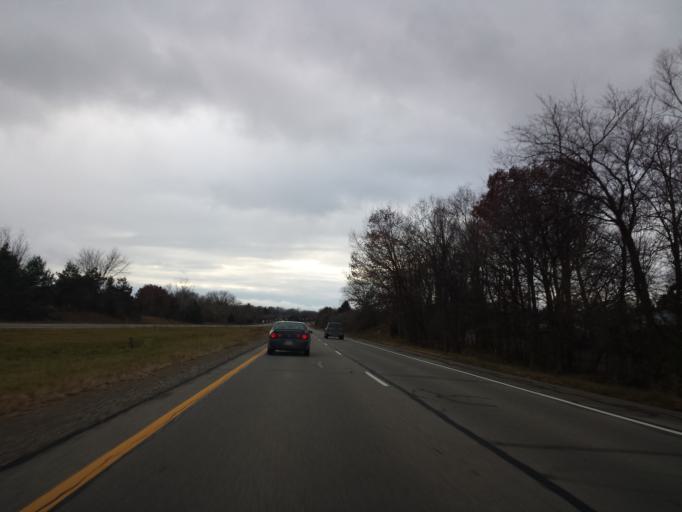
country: US
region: Michigan
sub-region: Ingham County
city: East Lansing
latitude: 42.7504
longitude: -84.4525
